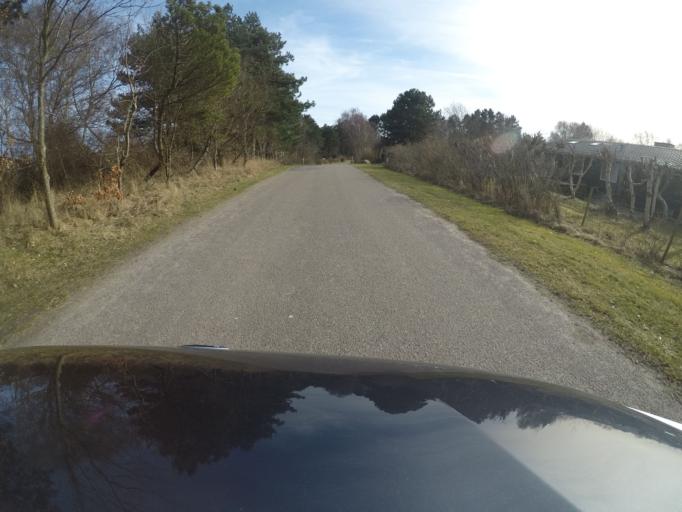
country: DK
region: Capital Region
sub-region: Halsnaes Kommune
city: Liseleje
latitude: 55.9963
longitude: 11.9197
